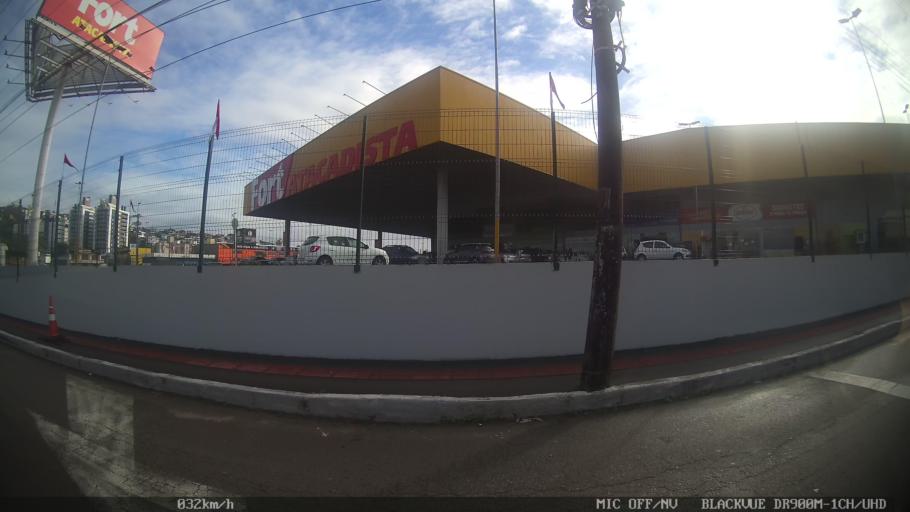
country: BR
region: Santa Catarina
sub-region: Sao Jose
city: Campinas
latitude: -27.5914
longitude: -48.6169
